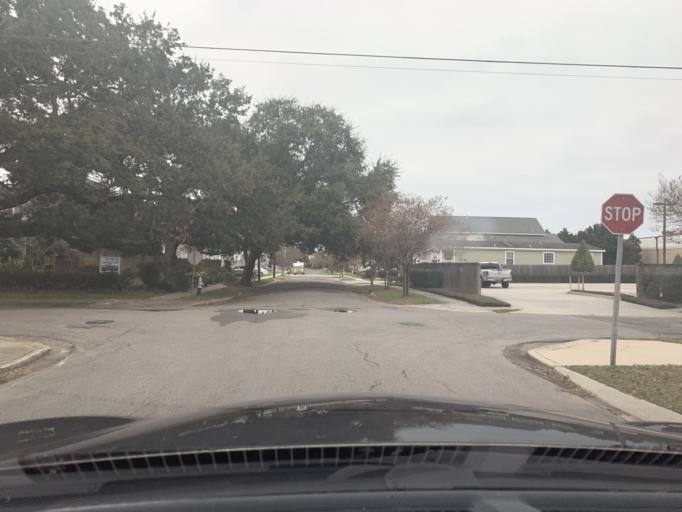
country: US
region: Louisiana
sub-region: Jefferson Parish
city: Metairie
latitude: 30.0176
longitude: -90.1078
